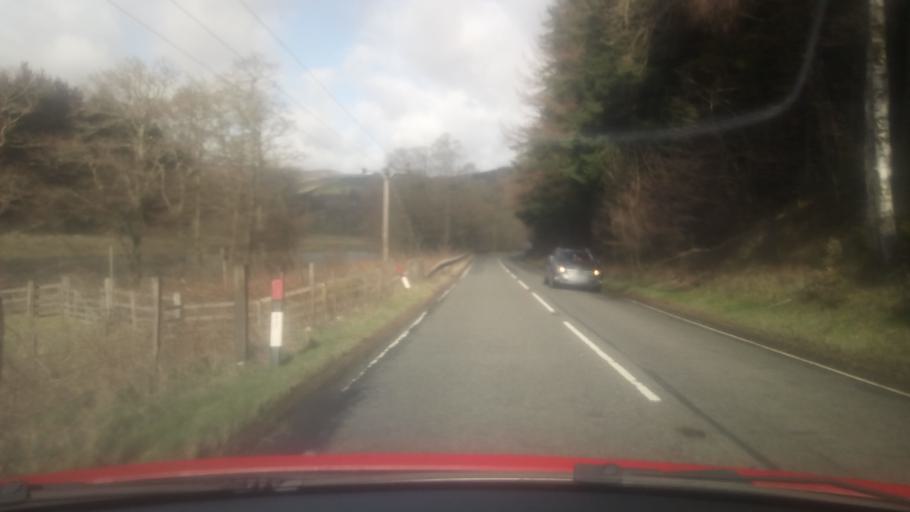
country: GB
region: Scotland
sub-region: The Scottish Borders
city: Innerleithen
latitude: 55.6209
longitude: -2.9562
